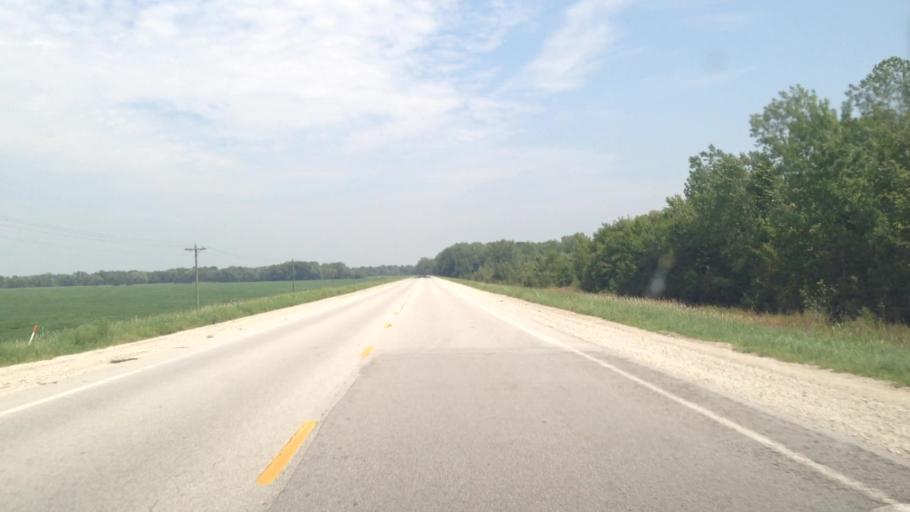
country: US
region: Kansas
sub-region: Neosho County
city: Erie
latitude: 37.5519
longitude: -95.2618
